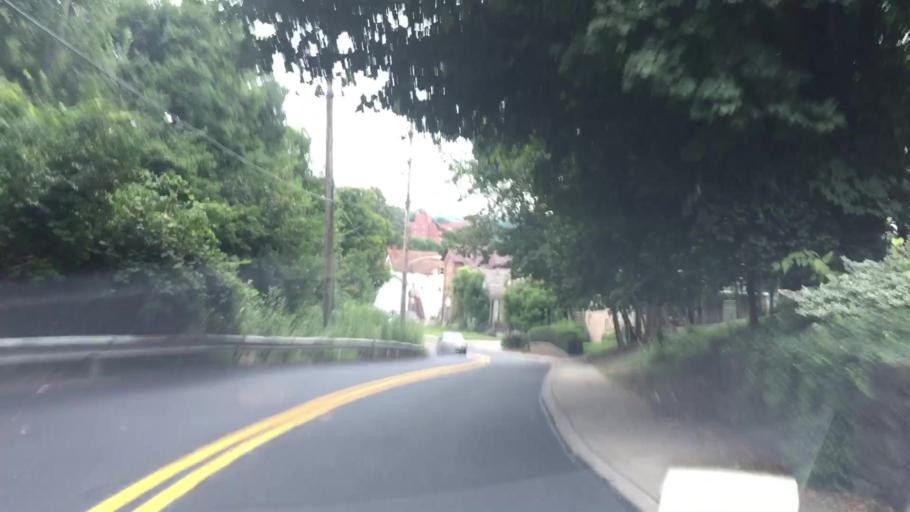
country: US
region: Pennsylvania
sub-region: Allegheny County
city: Carnegie
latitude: 40.4088
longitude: -80.0913
